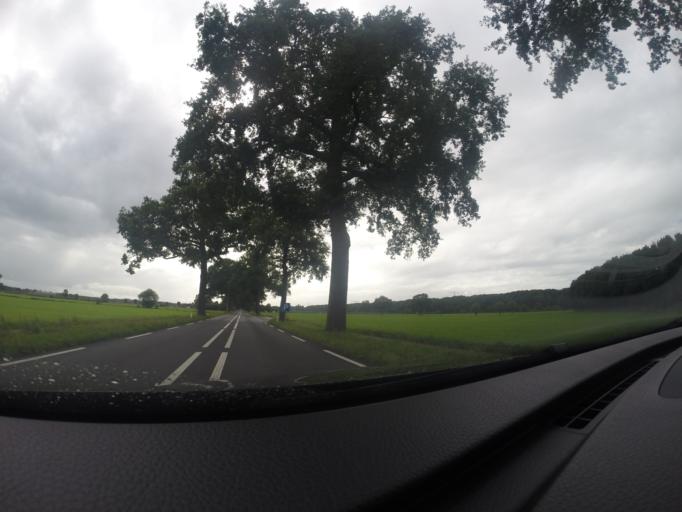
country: NL
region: Overijssel
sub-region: Gemeente Hof van Twente
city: Markelo
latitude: 52.1816
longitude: 6.4828
